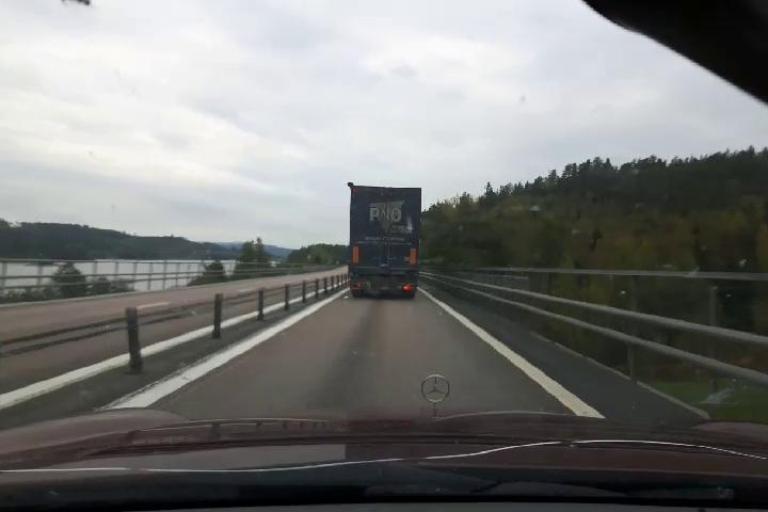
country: SE
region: Vaesternorrland
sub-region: Haernoesands Kommun
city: Haernoesand
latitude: 62.8244
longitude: 17.9697
